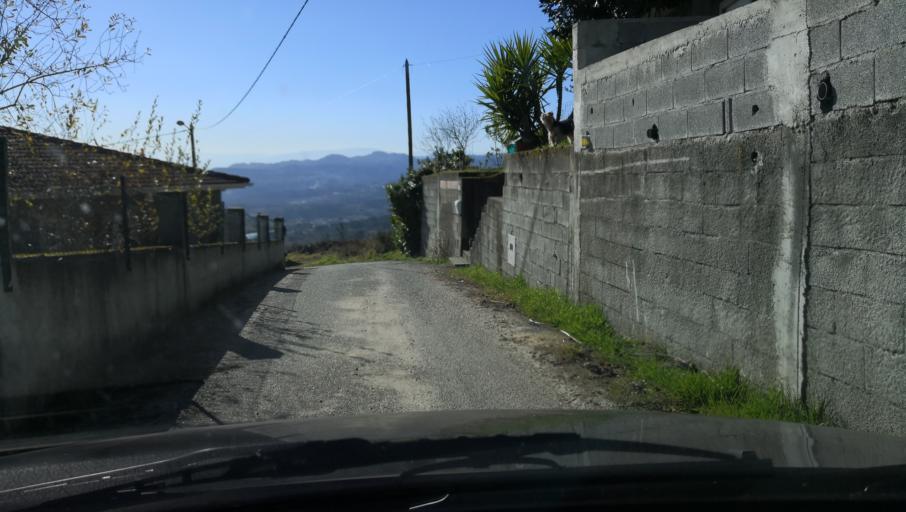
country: PT
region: Vila Real
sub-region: Vila Real
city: Vila Real
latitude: 41.3280
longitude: -7.7609
